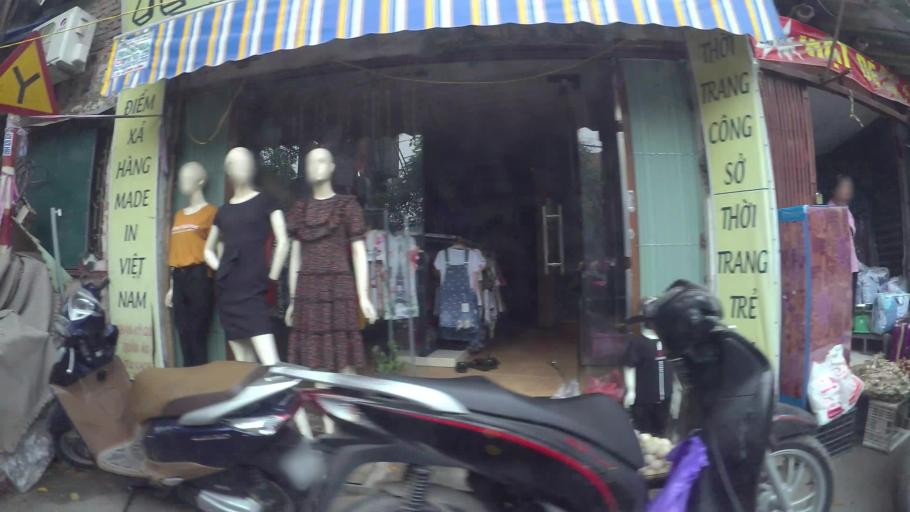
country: VN
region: Ha Noi
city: Hai BaTrung
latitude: 20.9876
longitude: 105.8885
